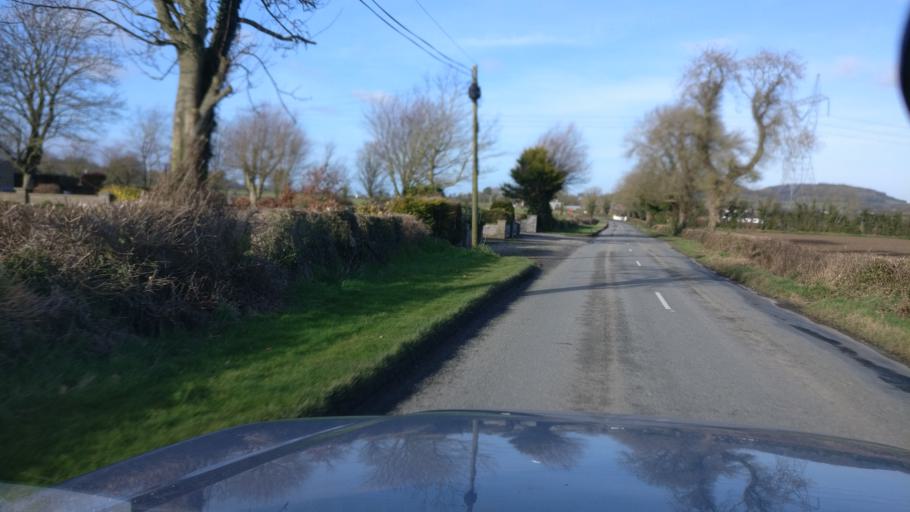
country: IE
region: Leinster
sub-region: Laois
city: Stradbally
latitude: 52.9915
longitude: -7.2206
